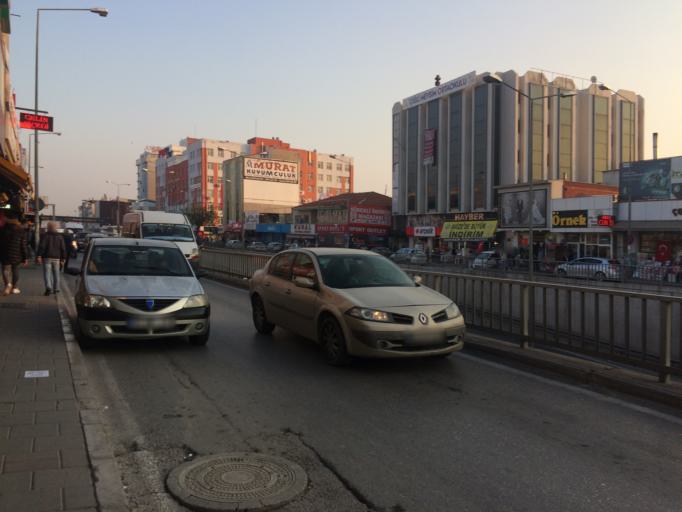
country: TR
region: Izmir
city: Karsiyaka
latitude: 38.4933
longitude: 27.0634
